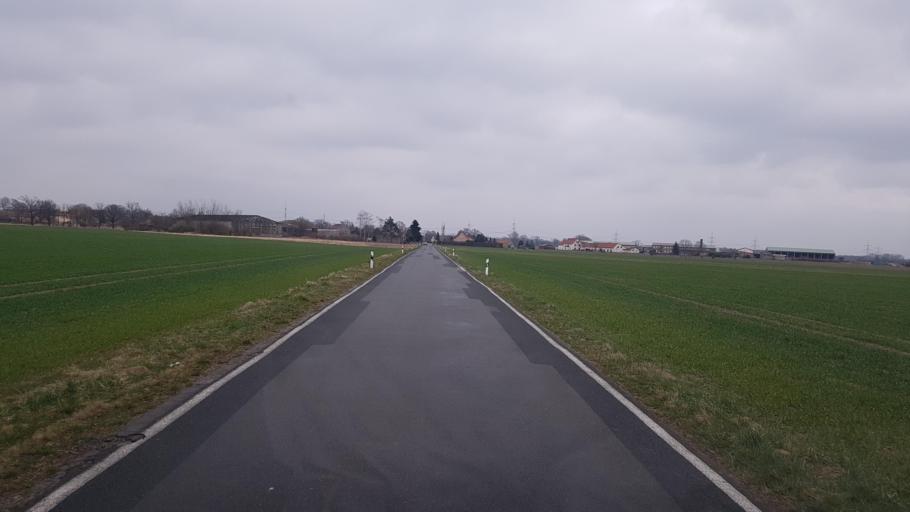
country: DE
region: Saxony
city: Nauwalde
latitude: 51.4227
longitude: 13.3791
